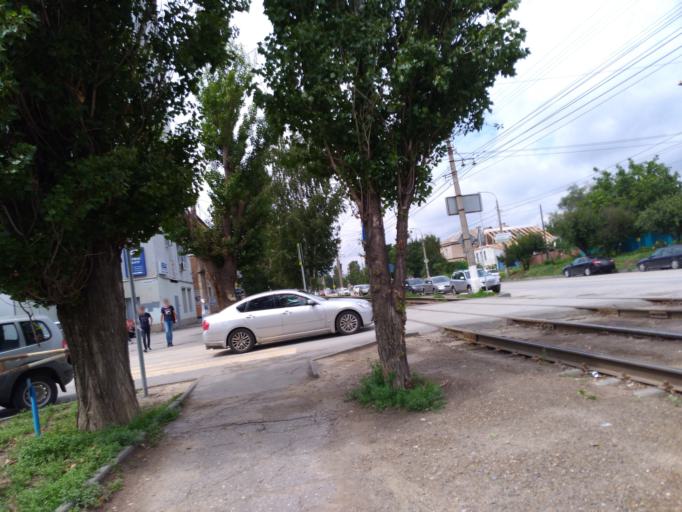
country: RU
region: Volgograd
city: Volgograd
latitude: 48.7161
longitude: 44.4877
